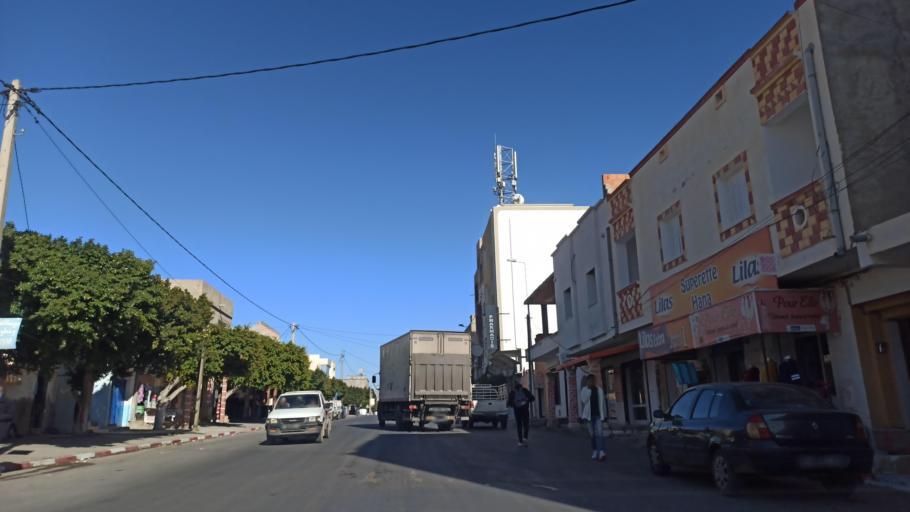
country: TN
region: Sidi Bu Zayd
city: Bi'r al Hufayy
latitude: 34.9330
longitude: 9.1967
